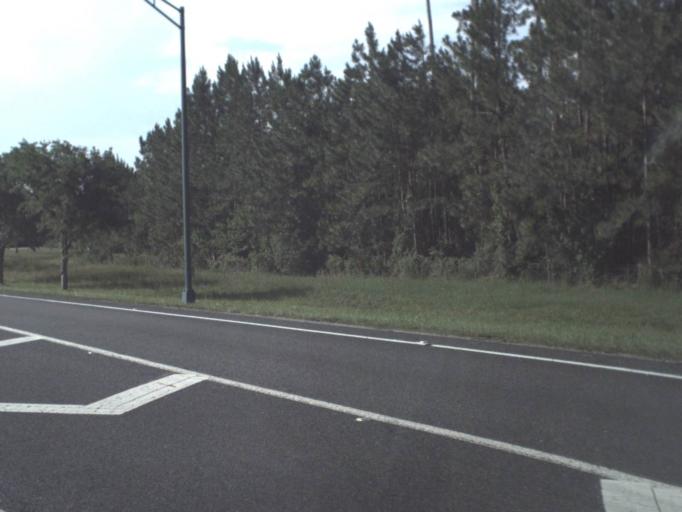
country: US
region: Florida
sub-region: Saint Johns County
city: Villano Beach
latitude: 29.9826
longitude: -81.4596
